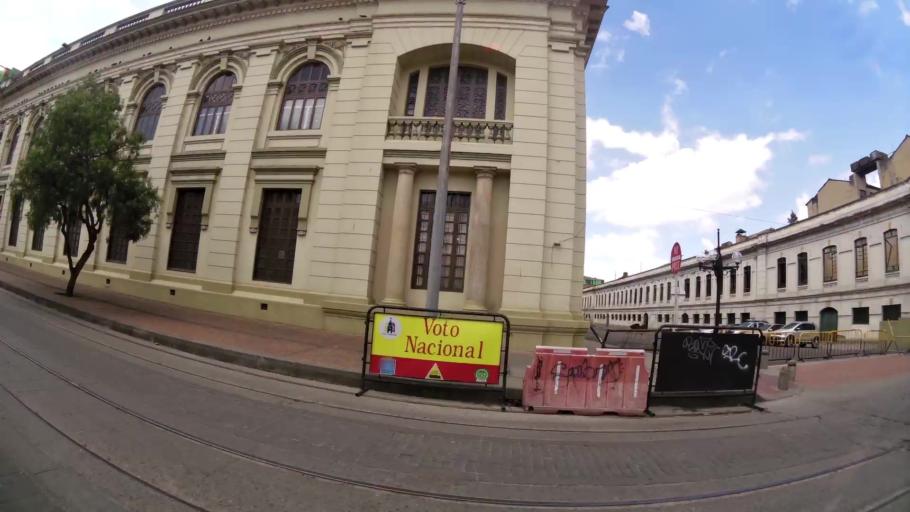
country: CO
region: Bogota D.C.
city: Bogota
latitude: 4.6016
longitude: -74.0824
